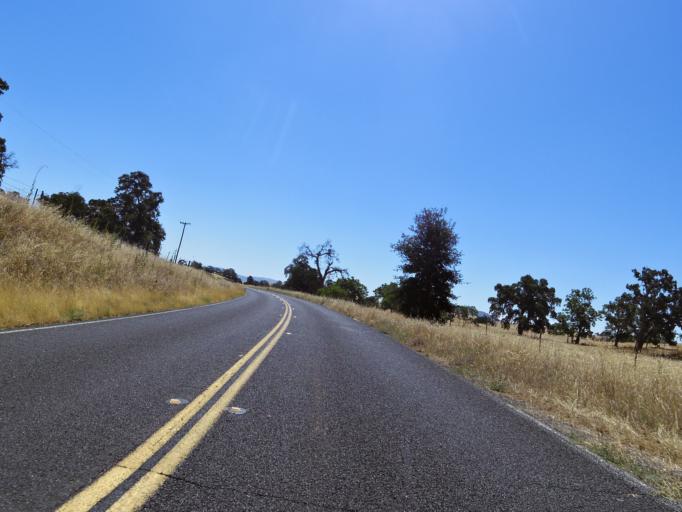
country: US
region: California
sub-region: Merced County
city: Planada
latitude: 37.4872
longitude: -120.2132
